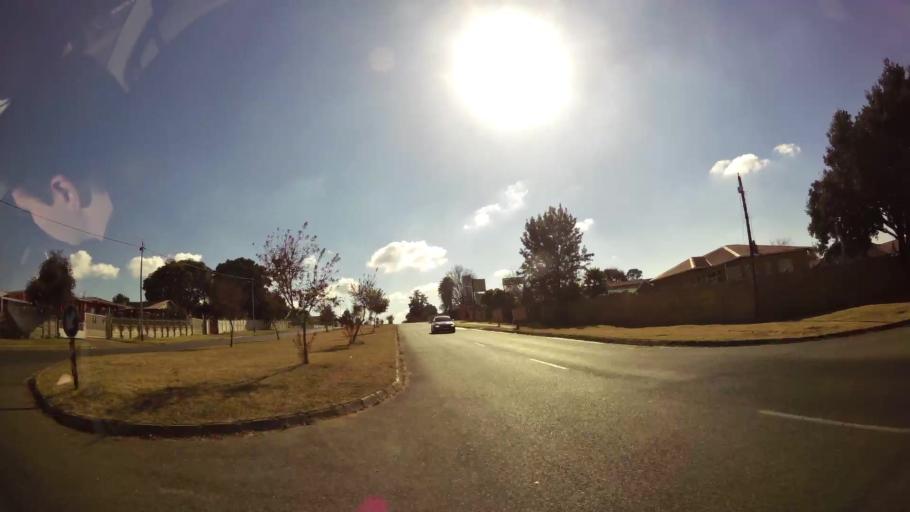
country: ZA
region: Gauteng
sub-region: City of Johannesburg Metropolitan Municipality
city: Roodepoort
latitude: -26.1479
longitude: 27.8338
